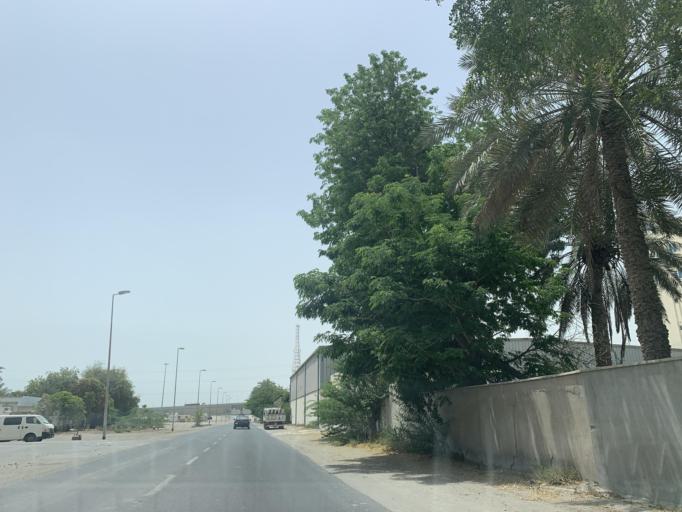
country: BH
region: Northern
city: Ar Rifa'
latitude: 26.1286
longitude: 50.5922
